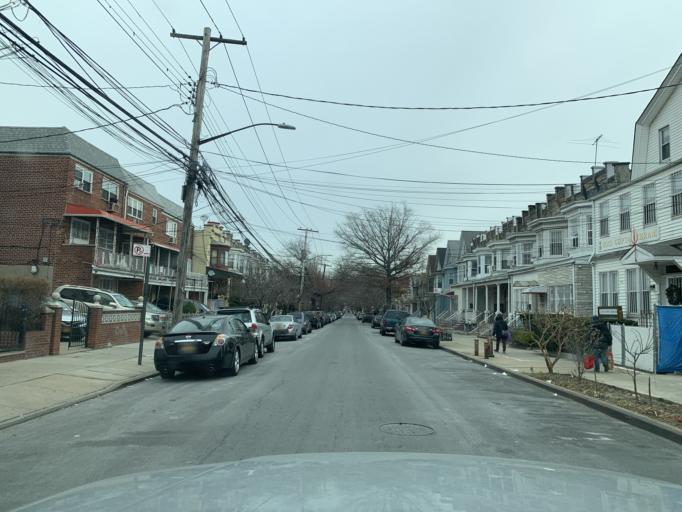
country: US
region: New York
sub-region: Queens County
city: Borough of Queens
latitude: 40.7396
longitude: -73.8737
